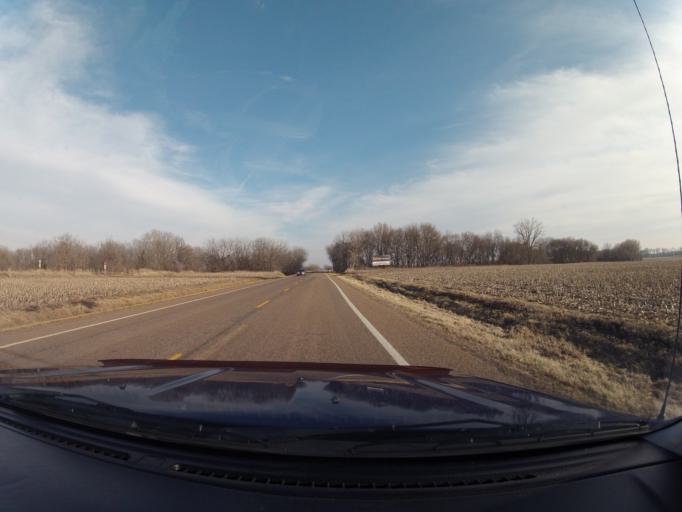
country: US
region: Kansas
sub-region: Pottawatomie County
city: Saint Marys
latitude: 39.2137
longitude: -96.1159
